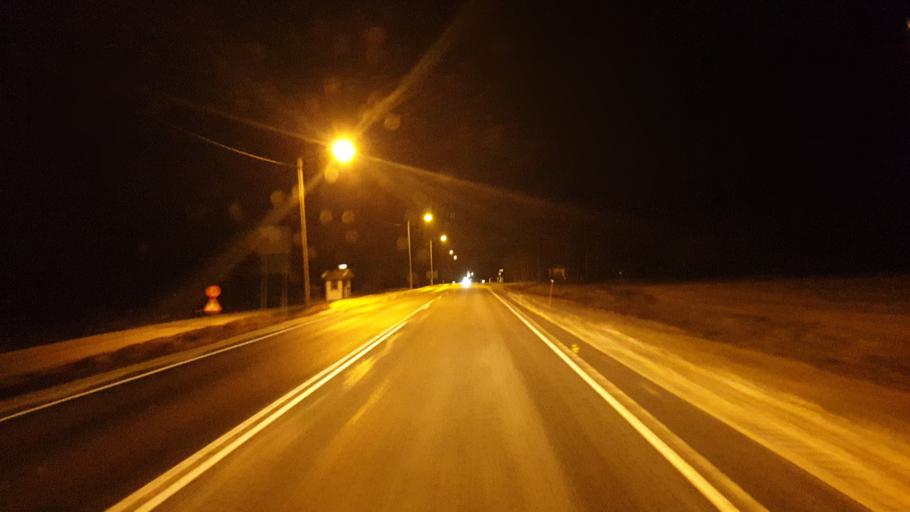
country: FI
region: Central Finland
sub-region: AEaenekoski
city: AEaenekoski
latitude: 62.7479
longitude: 25.7741
